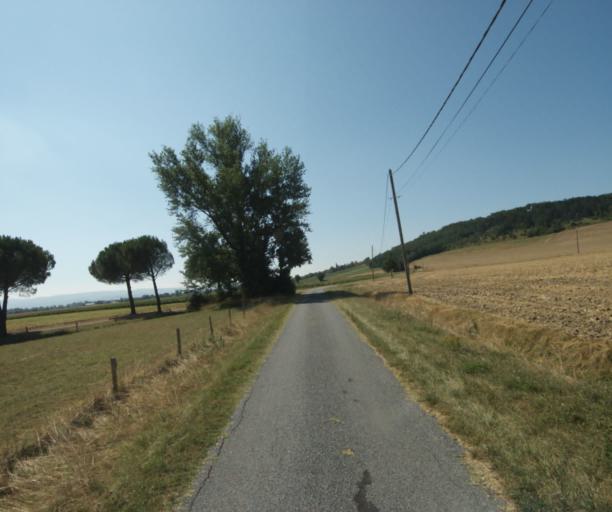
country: FR
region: Midi-Pyrenees
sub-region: Departement de la Haute-Garonne
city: Revel
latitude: 43.5181
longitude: 1.9494
